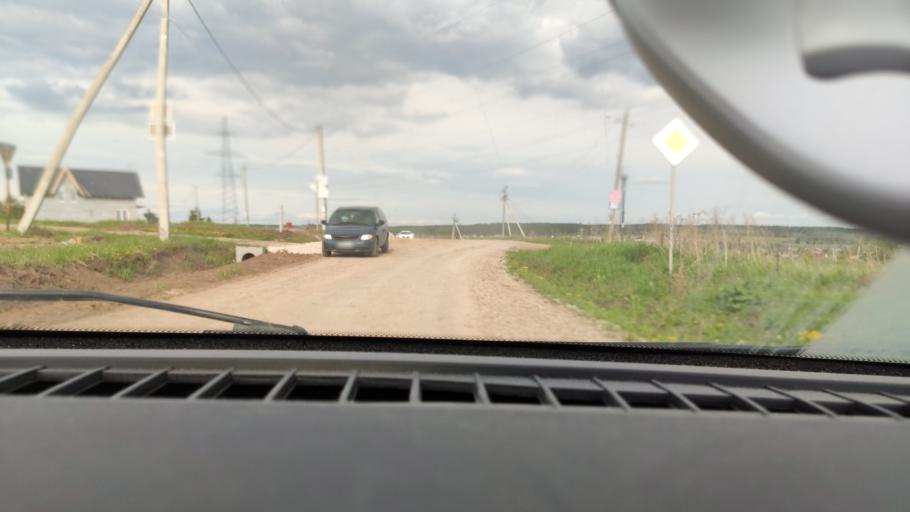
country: RU
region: Perm
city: Ferma
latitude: 57.9414
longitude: 56.3420
